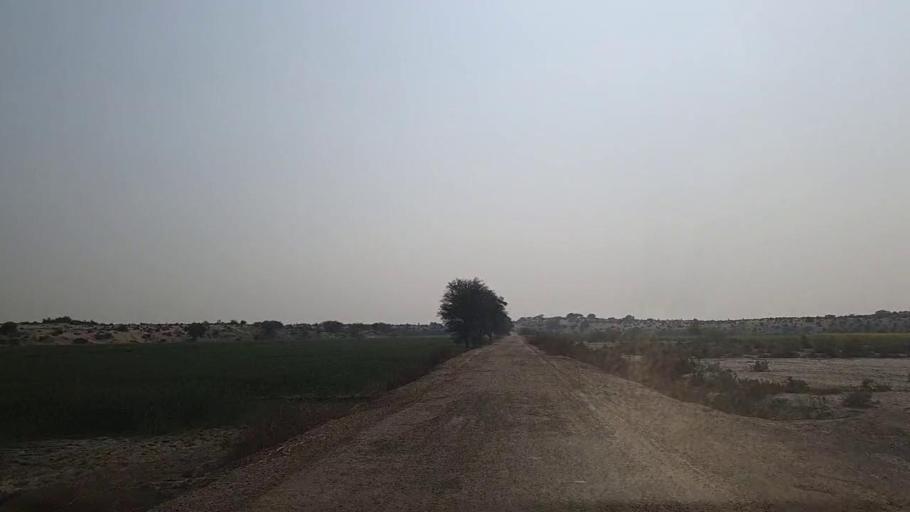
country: PK
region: Sindh
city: Jam Sahib
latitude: 26.4491
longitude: 68.5233
